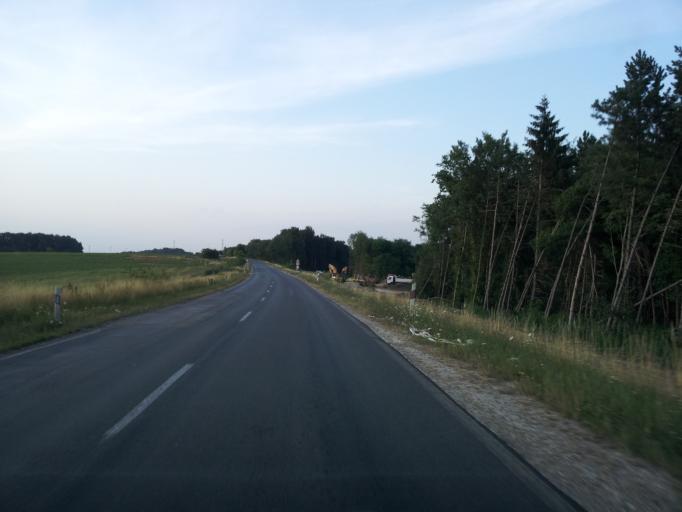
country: HU
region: Zala
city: Zalalovo
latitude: 46.8191
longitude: 16.5798
